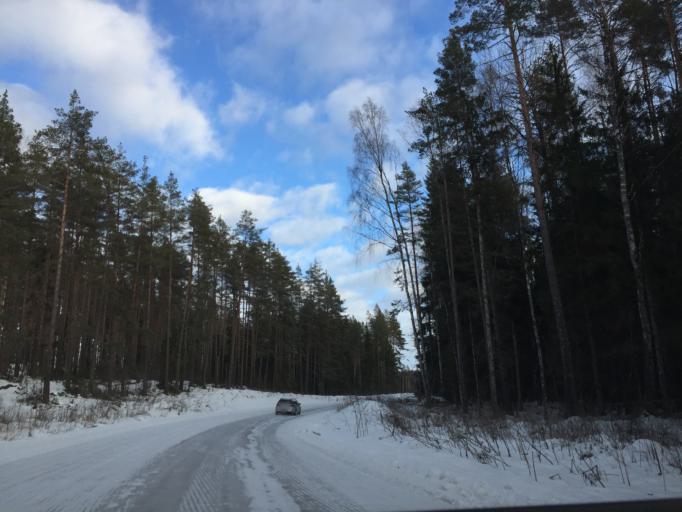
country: LV
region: Ogre
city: Jumprava
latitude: 56.5764
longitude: 24.9426
